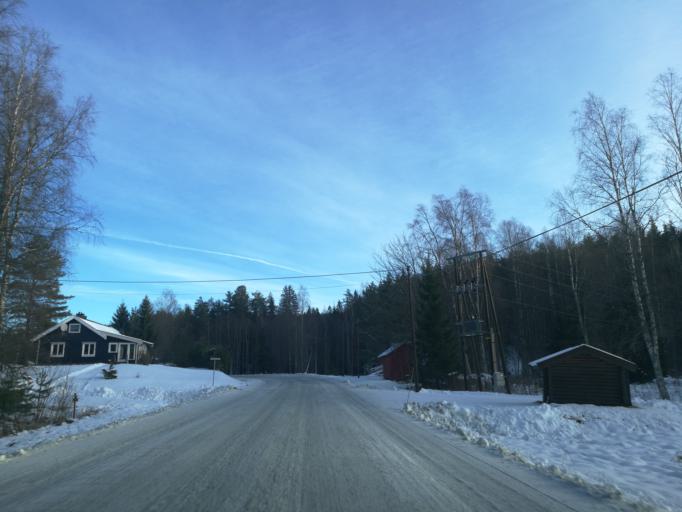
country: NO
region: Hedmark
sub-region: Grue
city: Kirkenaer
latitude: 60.3307
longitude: 12.2906
